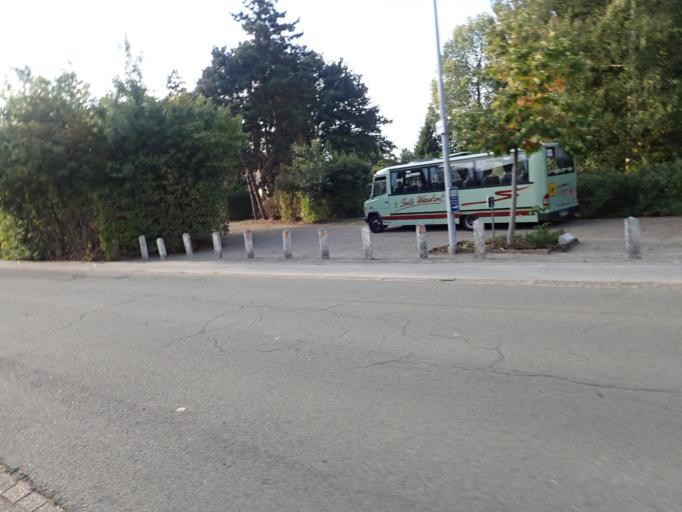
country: BE
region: Flanders
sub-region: Provincie Oost-Vlaanderen
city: Sint-Niklaas
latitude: 51.1774
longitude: 4.1865
